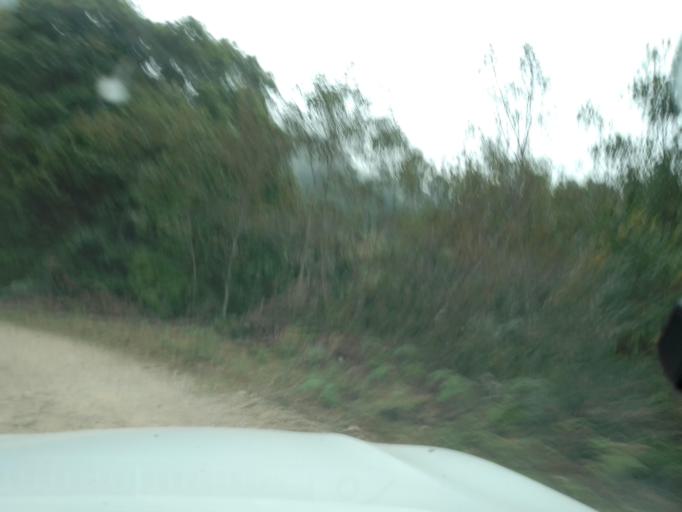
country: MX
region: Chiapas
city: Motozintla de Mendoza
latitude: 15.2160
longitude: -92.2203
